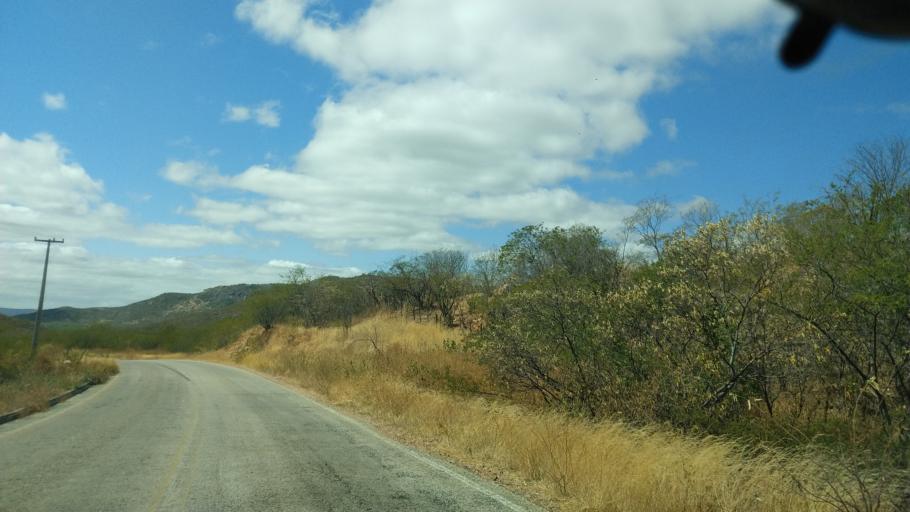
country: BR
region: Rio Grande do Norte
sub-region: Currais Novos
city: Currais Novos
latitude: -6.2635
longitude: -36.5950
